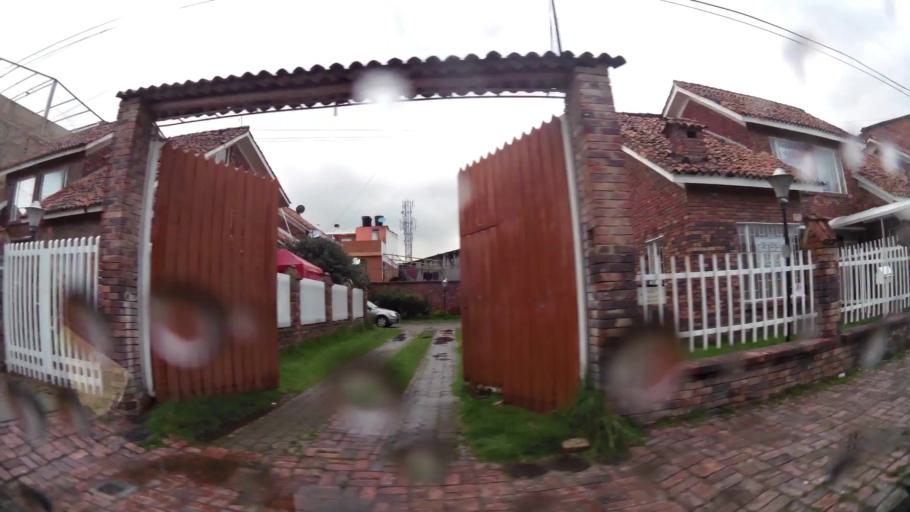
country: CO
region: Cundinamarca
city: Chia
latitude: 4.8672
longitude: -74.0539
